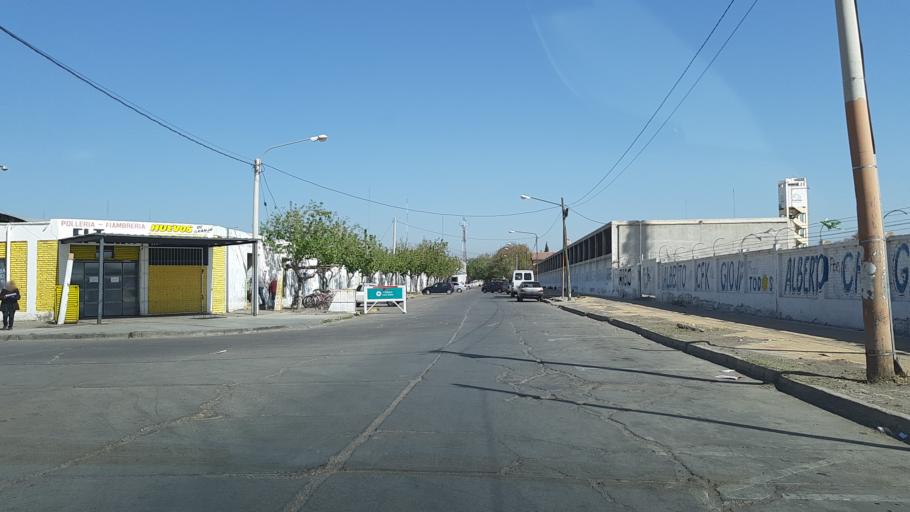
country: AR
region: San Juan
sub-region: Departamento de Santa Lucia
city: Santa Lucia
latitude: -31.5290
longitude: -68.5129
